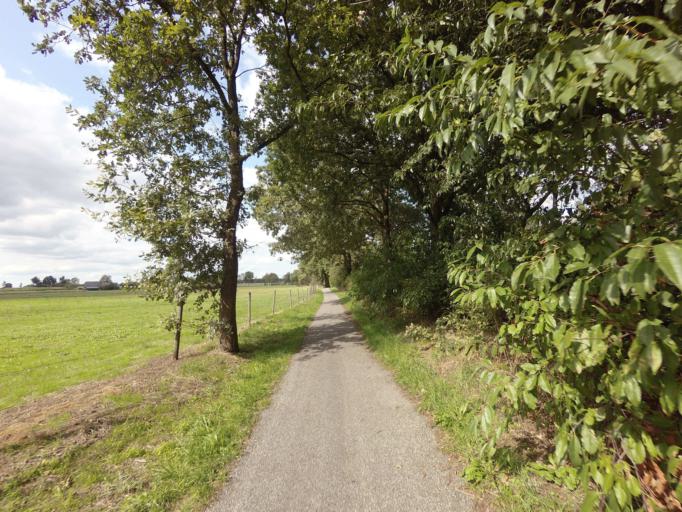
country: NL
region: Drenthe
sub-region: Gemeente De Wolden
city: Ruinen
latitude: 52.7734
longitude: 6.3652
